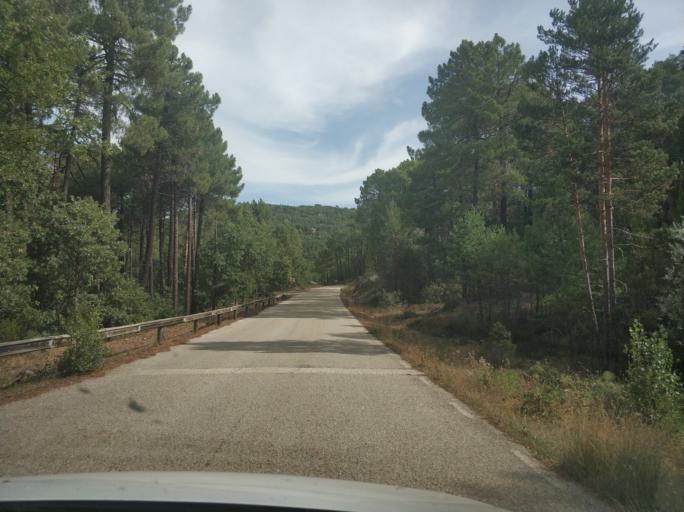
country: ES
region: Castille and Leon
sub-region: Provincia de Soria
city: Duruelo de la Sierra
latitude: 41.8970
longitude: -2.9430
